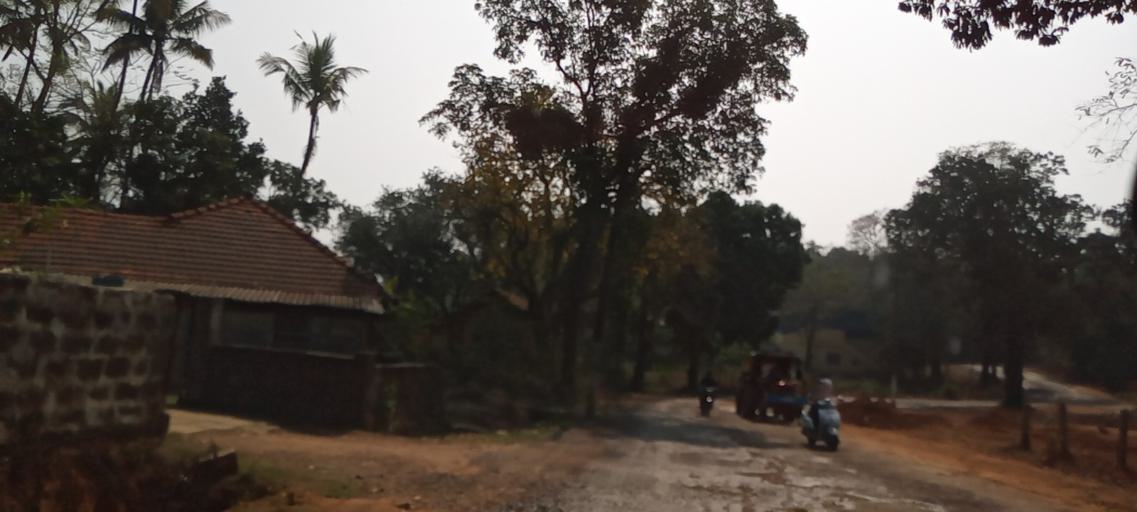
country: IN
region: Karnataka
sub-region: Udupi
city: Someshwar
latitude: 13.5269
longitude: 74.9259
